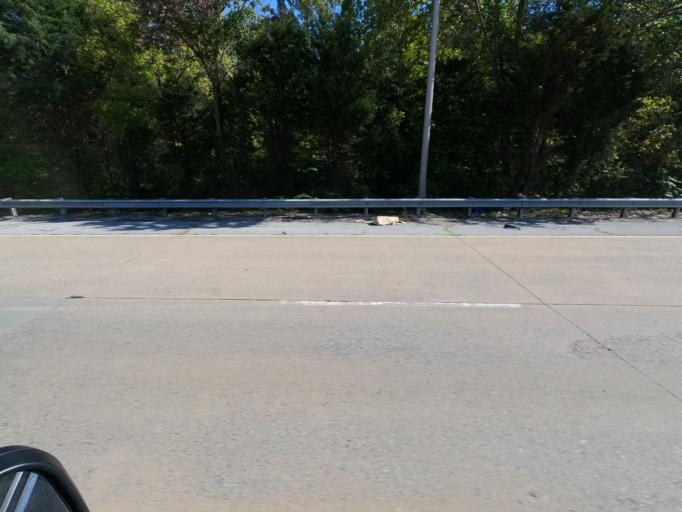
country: US
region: Tennessee
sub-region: Hamblen County
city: Morristown
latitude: 36.2324
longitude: -83.2604
